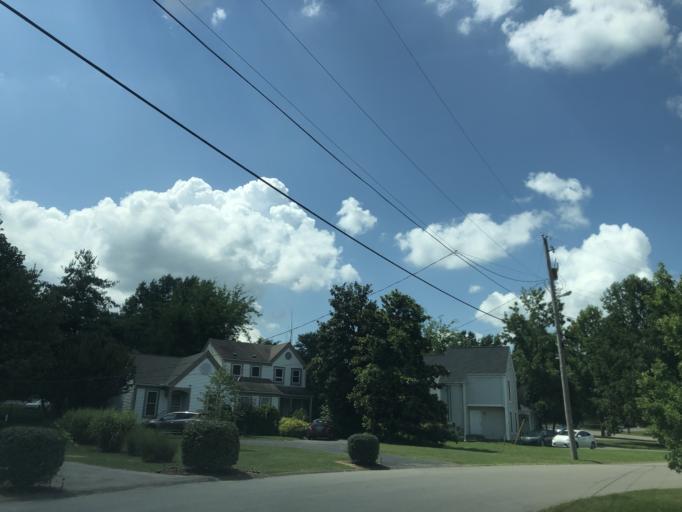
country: US
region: Tennessee
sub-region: Davidson County
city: Lakewood
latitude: 36.2043
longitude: -86.6048
